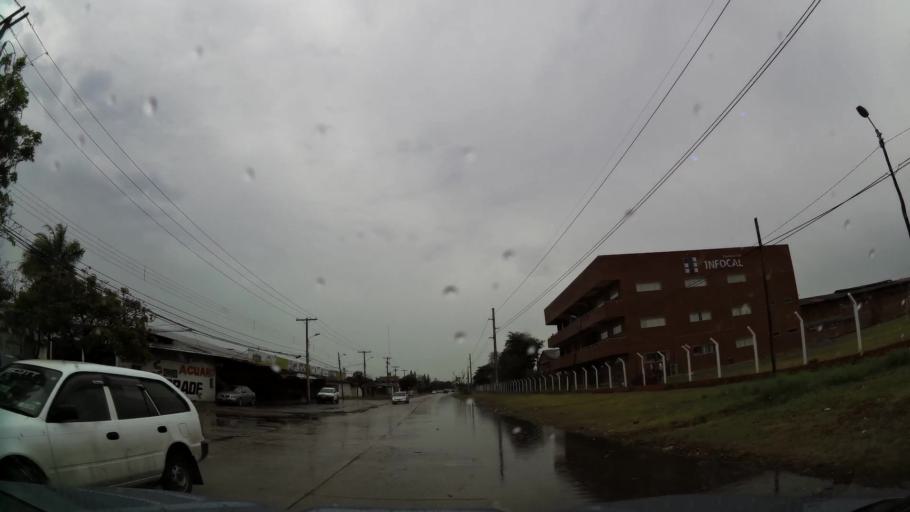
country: BO
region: Santa Cruz
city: Santa Cruz de la Sierra
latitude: -17.7778
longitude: -63.1533
